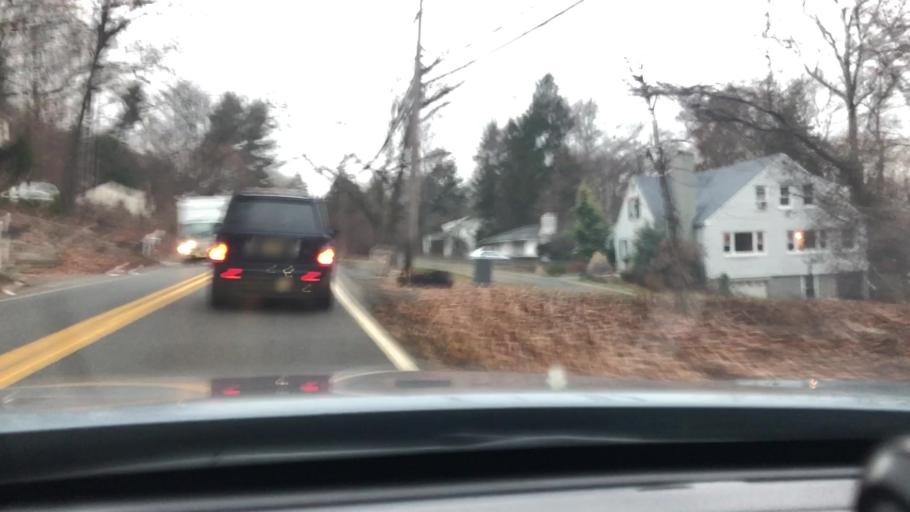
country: US
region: New Jersey
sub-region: Bergen County
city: Woodcliff Lake
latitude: 41.0020
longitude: -74.0753
